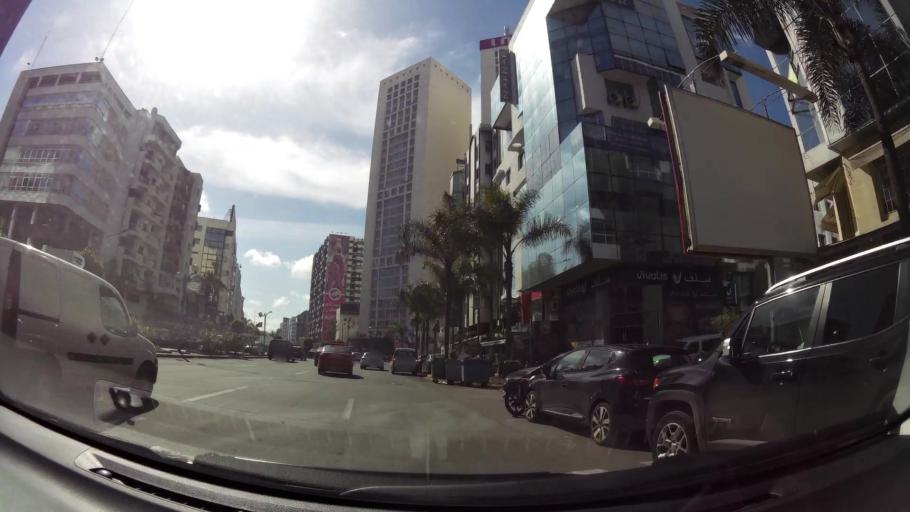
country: MA
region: Grand Casablanca
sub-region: Casablanca
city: Casablanca
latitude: 33.5879
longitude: -7.6331
